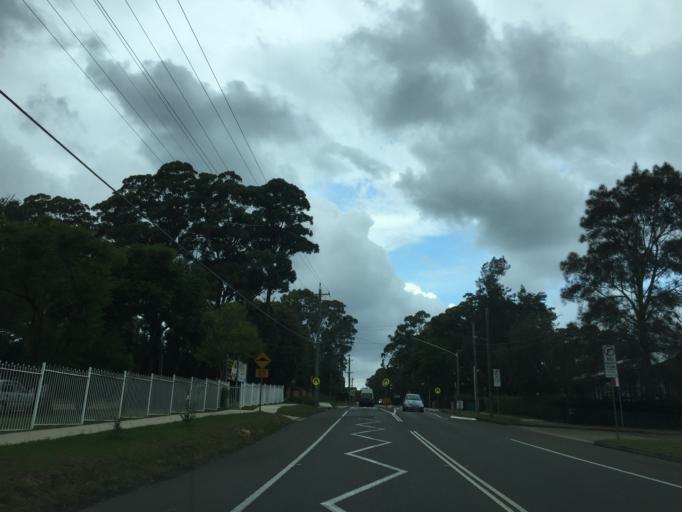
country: AU
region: New South Wales
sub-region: The Hills Shire
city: Glenhaven
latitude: -33.6998
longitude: 151.0032
